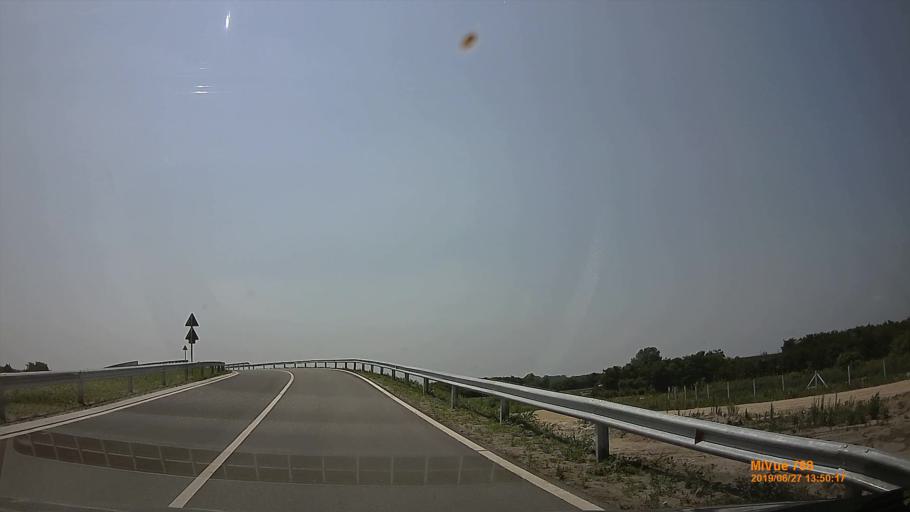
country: HU
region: Pest
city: Albertirsa
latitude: 47.2529
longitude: 19.6405
